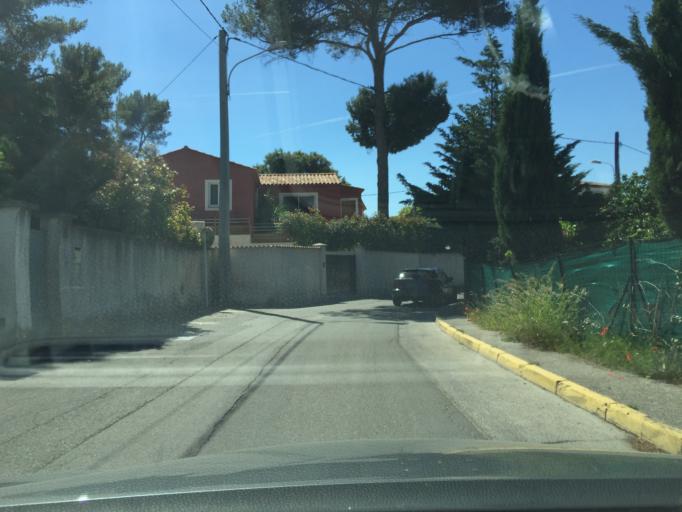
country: FR
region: Provence-Alpes-Cote d'Azur
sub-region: Departement des Bouches-du-Rhone
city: La Penne-sur-Huveaune
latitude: 43.2744
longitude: 5.5302
